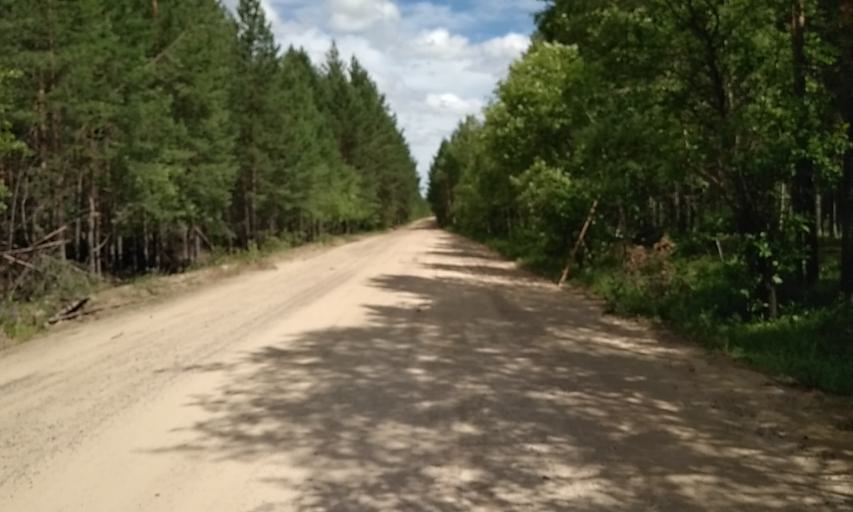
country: RU
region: Tomsk
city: Timiryazevskoye
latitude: 56.4198
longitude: 84.6778
